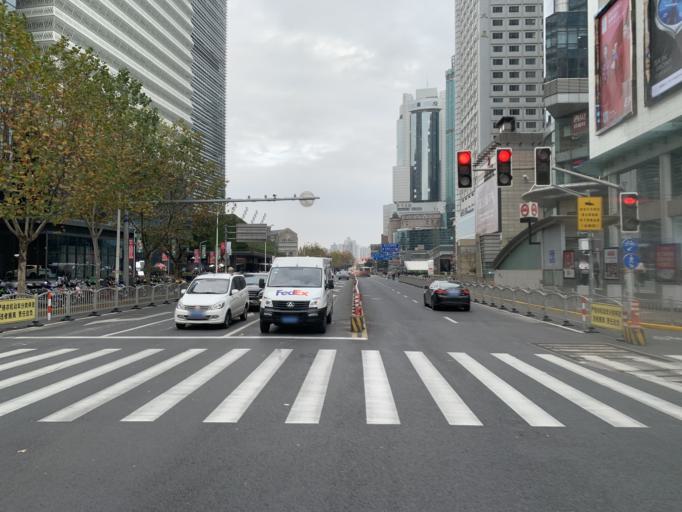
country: CN
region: Shanghai Shi
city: Pudong
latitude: 31.2320
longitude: 121.5114
